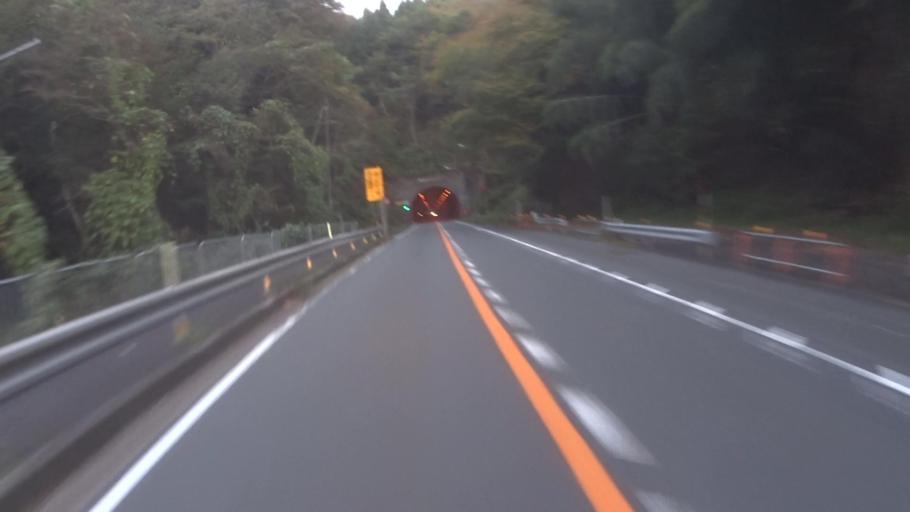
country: JP
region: Kyoto
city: Ayabe
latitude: 35.2420
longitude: 135.3149
